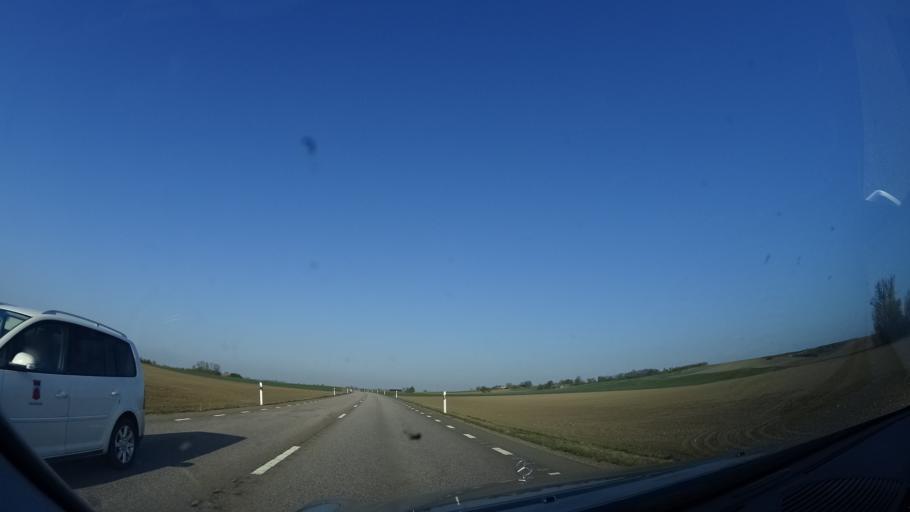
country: SE
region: Skane
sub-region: Eslovs Kommun
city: Eslov
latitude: 55.8689
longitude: 13.2063
